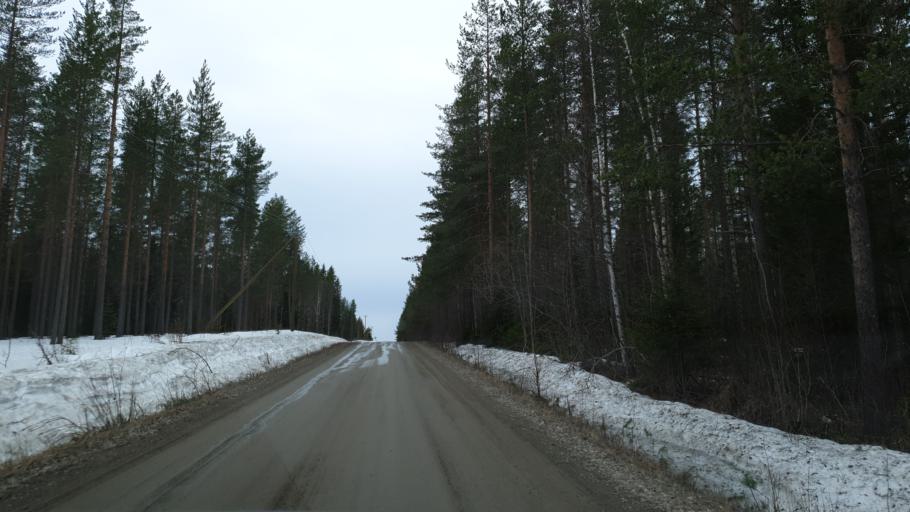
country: SE
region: Vaesterbotten
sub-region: Robertsfors Kommun
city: Robertsfors
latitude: 64.3937
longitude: 20.9912
